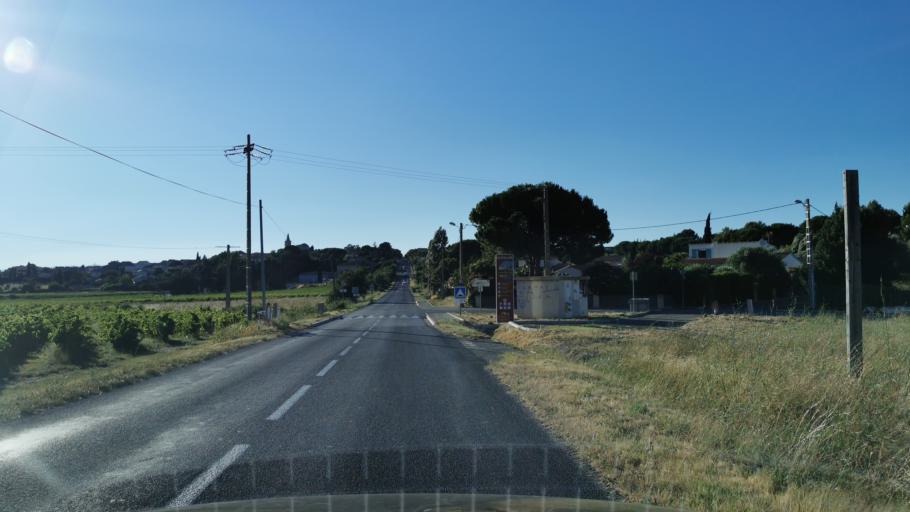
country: FR
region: Languedoc-Roussillon
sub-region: Departement de l'Aude
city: Ouveillan
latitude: 43.2834
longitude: 2.9786
